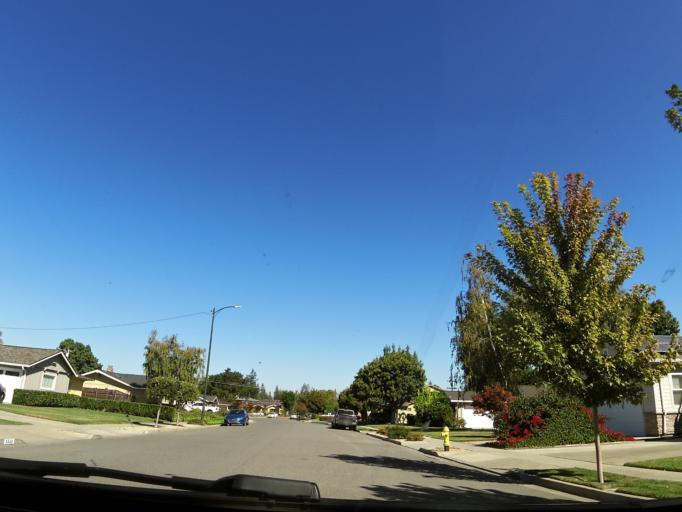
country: US
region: California
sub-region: Santa Clara County
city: Buena Vista
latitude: 37.2964
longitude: -121.9189
